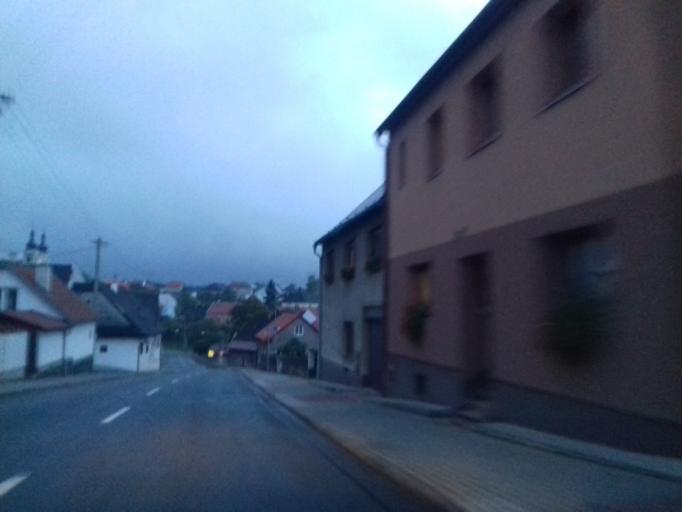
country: CZ
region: Pardubicky
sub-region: Okres Svitavy
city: Bystre
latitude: 49.6319
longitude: 16.3421
